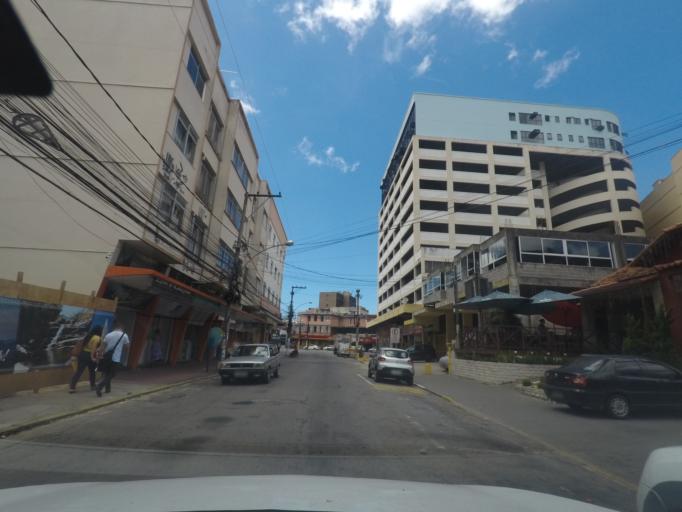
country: BR
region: Rio de Janeiro
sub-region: Teresopolis
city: Teresopolis
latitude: -22.4096
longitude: -42.9680
